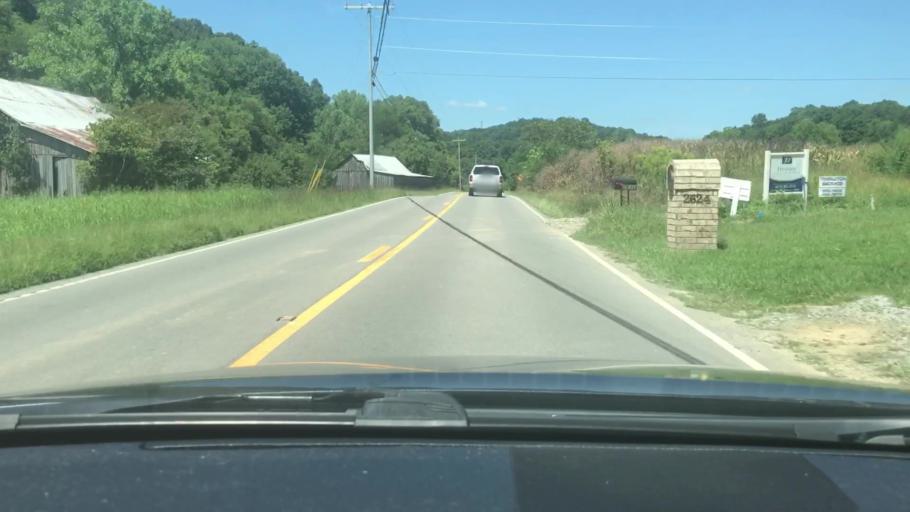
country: US
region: Tennessee
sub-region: Sumner County
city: White House
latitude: 36.4643
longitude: -86.5586
